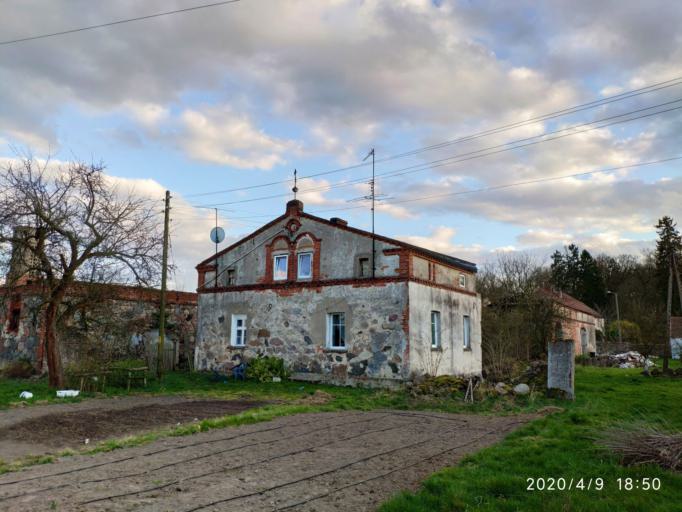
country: PL
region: Lubusz
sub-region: Powiat zielonogorski
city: Sulechow
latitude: 52.1304
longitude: 15.6863
